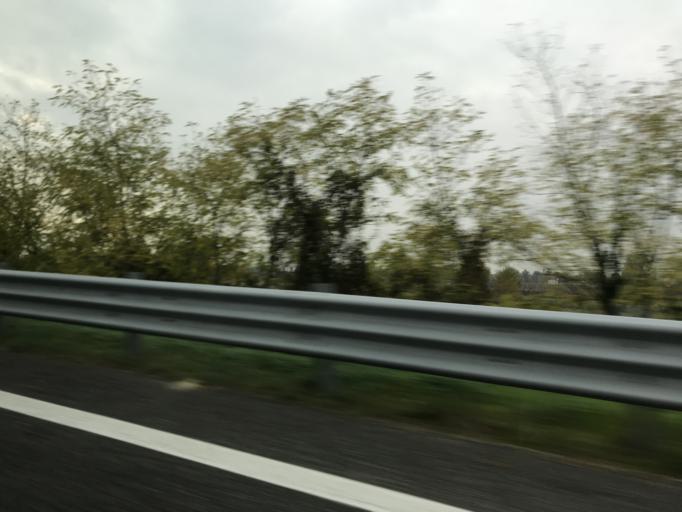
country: IT
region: Veneto
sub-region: Provincia di Venezia
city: Marcon-Gaggio-Colmello
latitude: 45.5820
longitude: 12.2884
